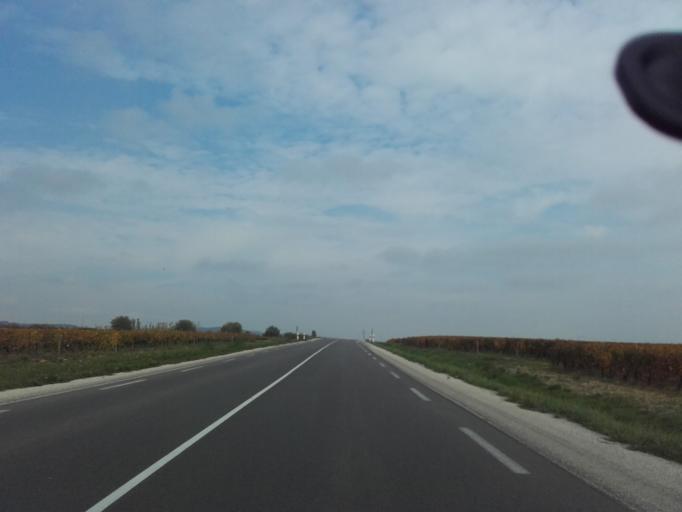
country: FR
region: Bourgogne
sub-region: Departement de la Cote-d'Or
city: Corpeau
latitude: 46.9507
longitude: 4.7642
